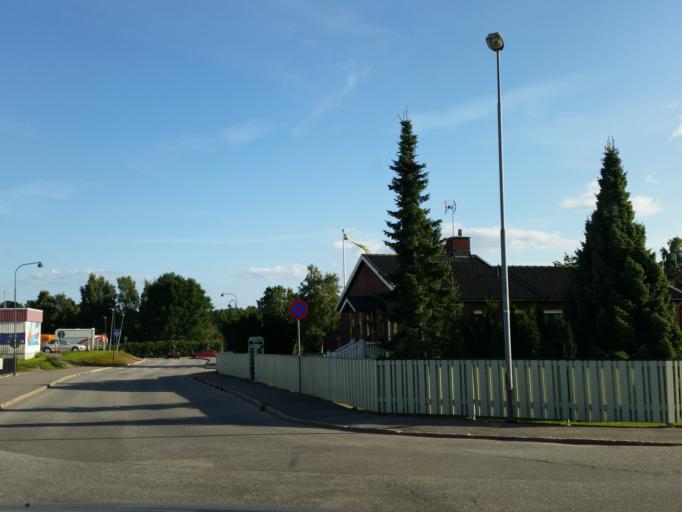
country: SE
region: Soedermanland
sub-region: Trosa Kommun
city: Vagnharad
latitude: 58.9457
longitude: 17.4870
